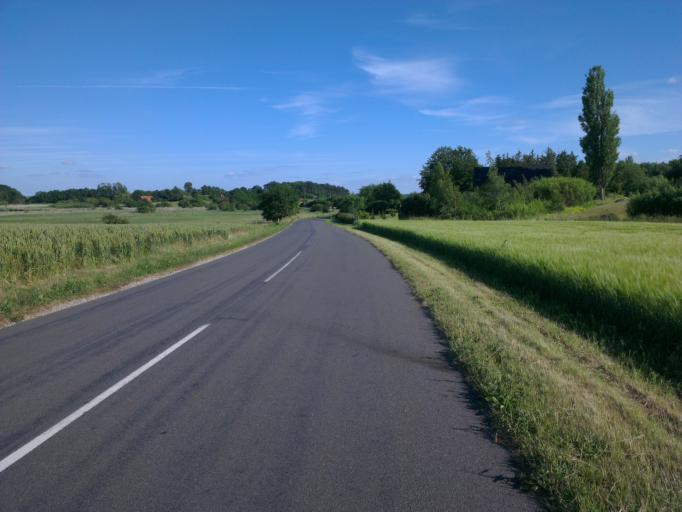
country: DK
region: Capital Region
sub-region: Frederikssund Kommune
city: Skibby
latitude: 55.7440
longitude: 11.9870
